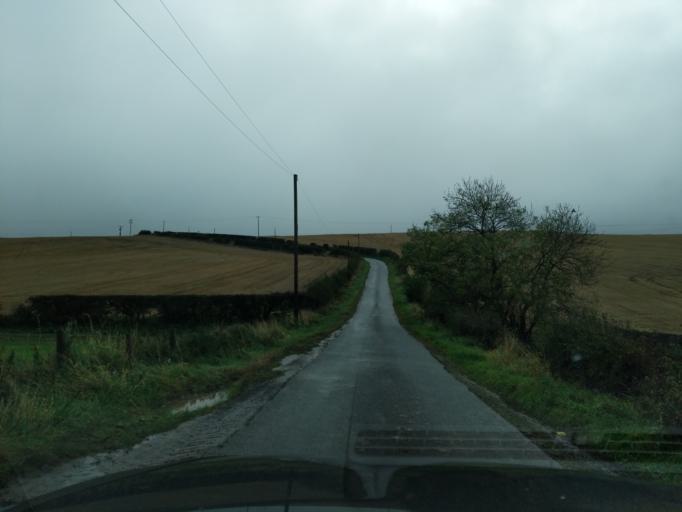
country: GB
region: Scotland
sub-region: East Lothian
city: Dunbar
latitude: 55.9468
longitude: -2.4026
